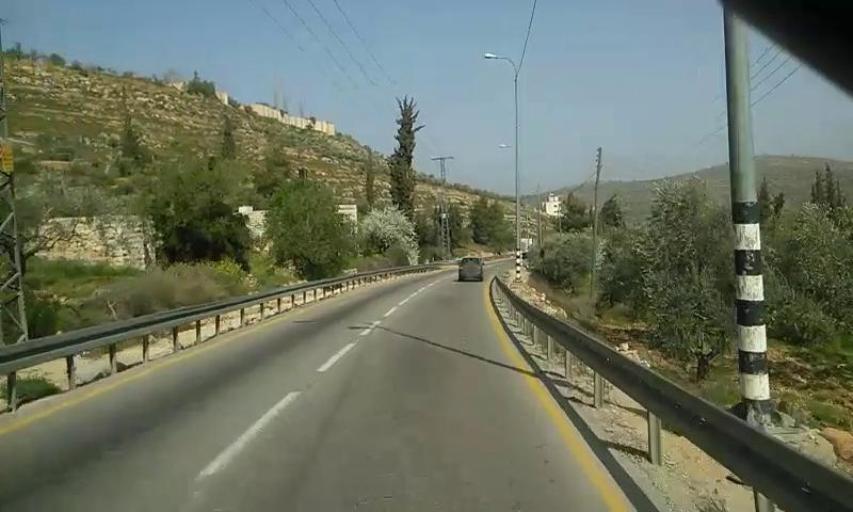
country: PS
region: West Bank
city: Sinjil
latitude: 32.0349
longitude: 35.2716
